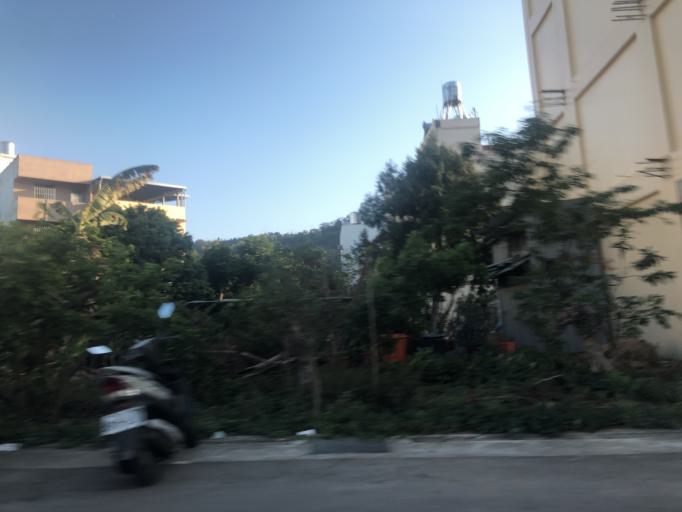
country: TW
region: Taiwan
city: Fengyuan
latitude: 24.2774
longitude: 120.7724
